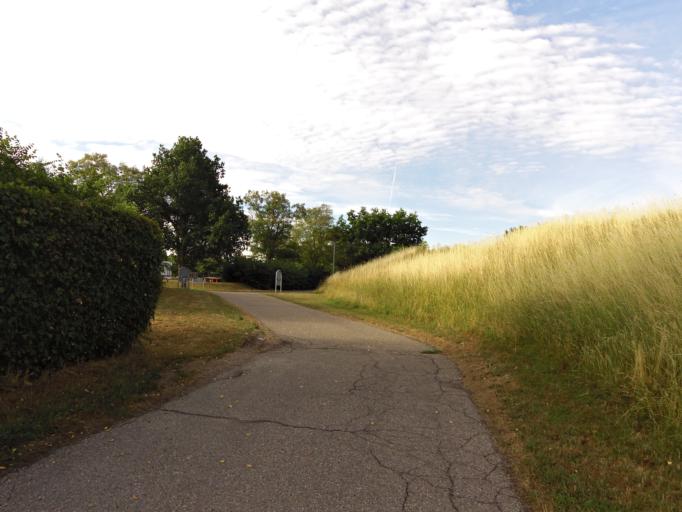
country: DK
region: Capital Region
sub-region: Fredensborg Kommune
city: Niva
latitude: 55.9416
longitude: 12.4887
